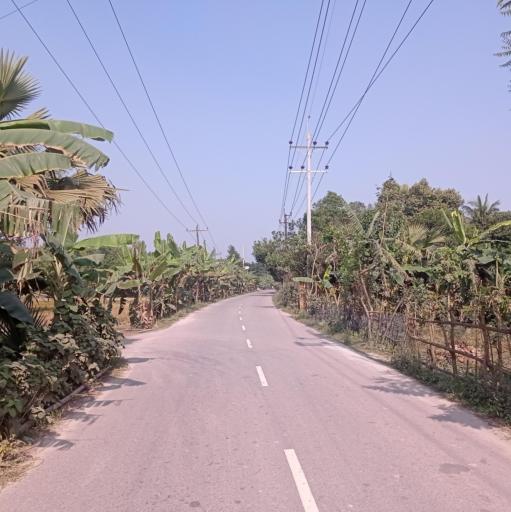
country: BD
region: Dhaka
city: Narsingdi
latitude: 24.0799
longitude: 90.6941
